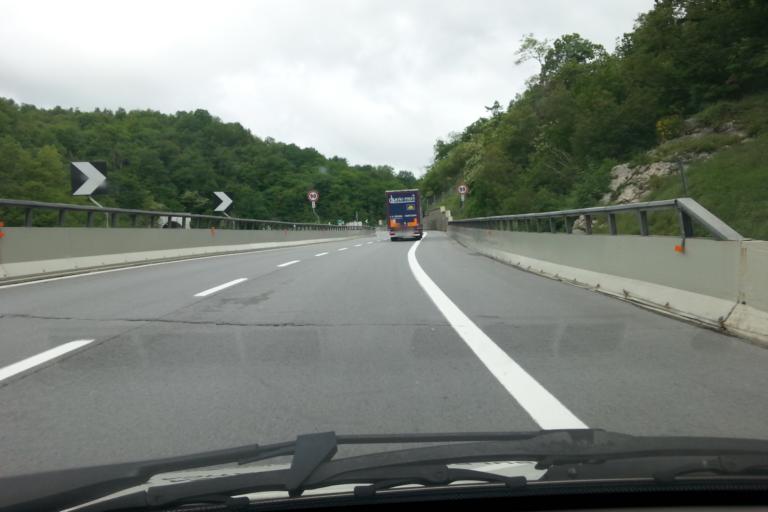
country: IT
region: Liguria
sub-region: Provincia di Savona
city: Valzemola
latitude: 44.3600
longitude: 8.1584
